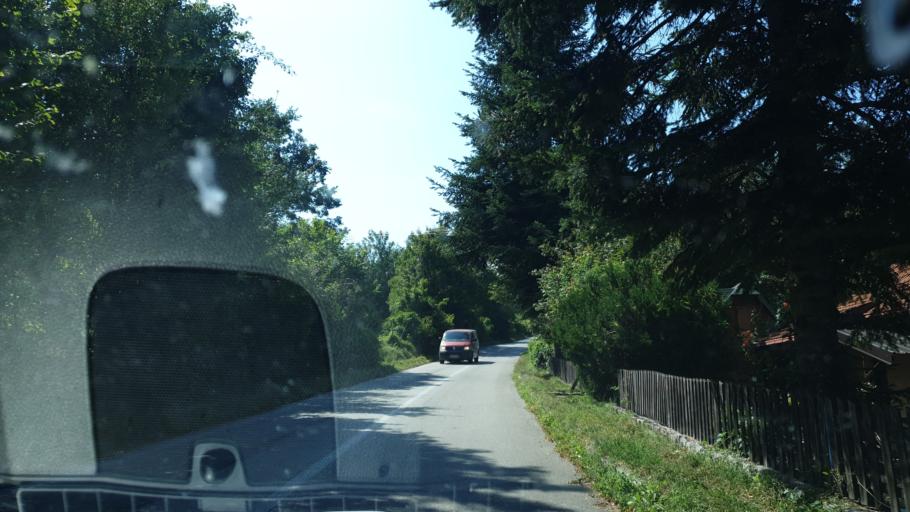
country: RS
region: Central Serbia
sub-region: Zlatiborski Okrug
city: Cajetina
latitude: 43.6974
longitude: 19.8544
